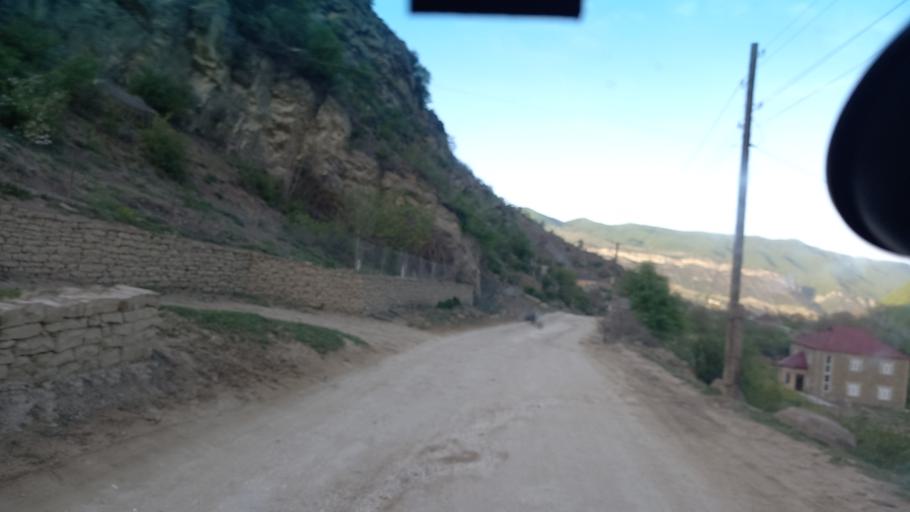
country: RU
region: Dagestan
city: Khuchni
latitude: 41.9710
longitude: 47.8782
